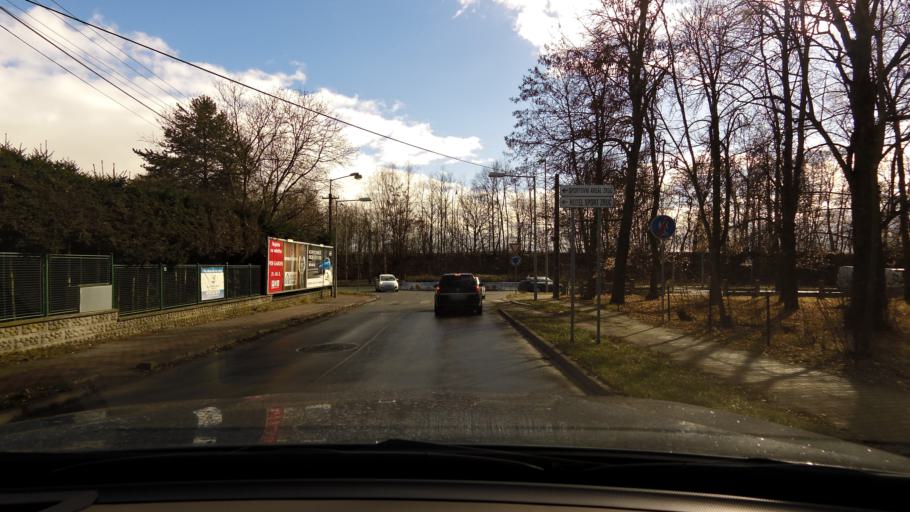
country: CZ
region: Plzensky
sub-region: Okres Plzen-Mesto
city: Pilsen
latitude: 49.7689
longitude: 13.4015
